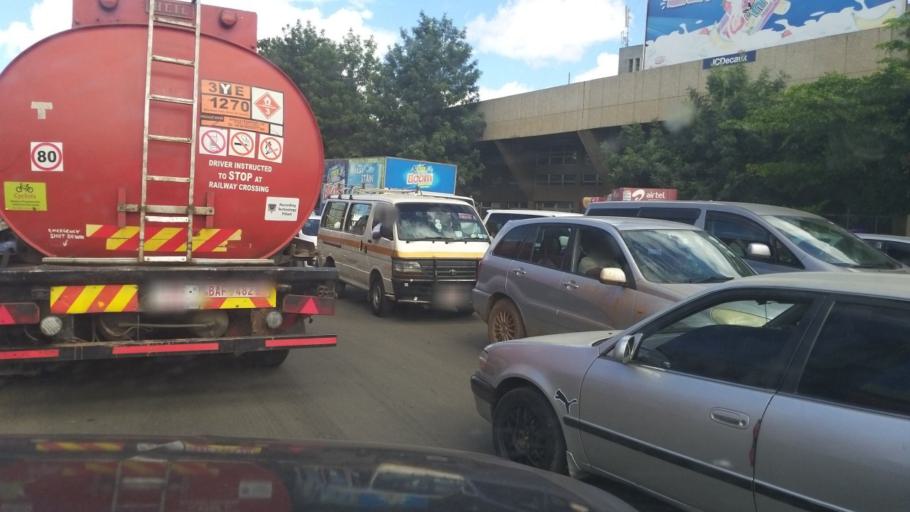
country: ZM
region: Lusaka
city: Lusaka
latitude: -15.4255
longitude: 28.2791
